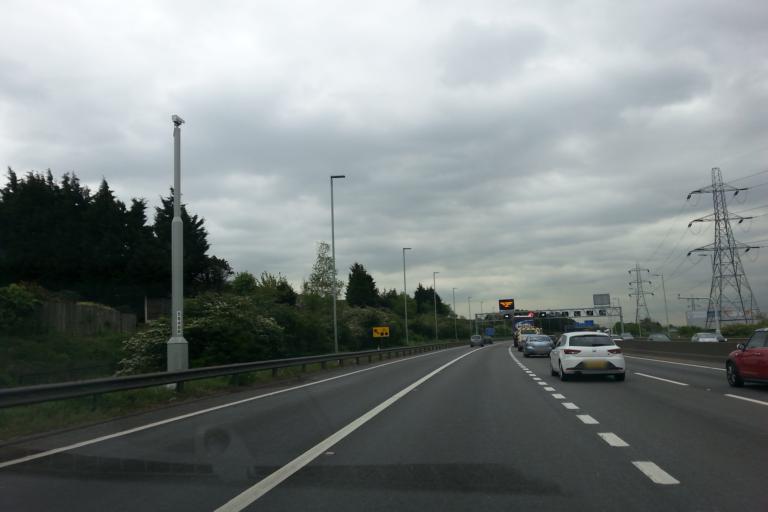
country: GB
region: England
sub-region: City and Borough of Birmingham
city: Birmingham
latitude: 52.5200
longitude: -1.8752
